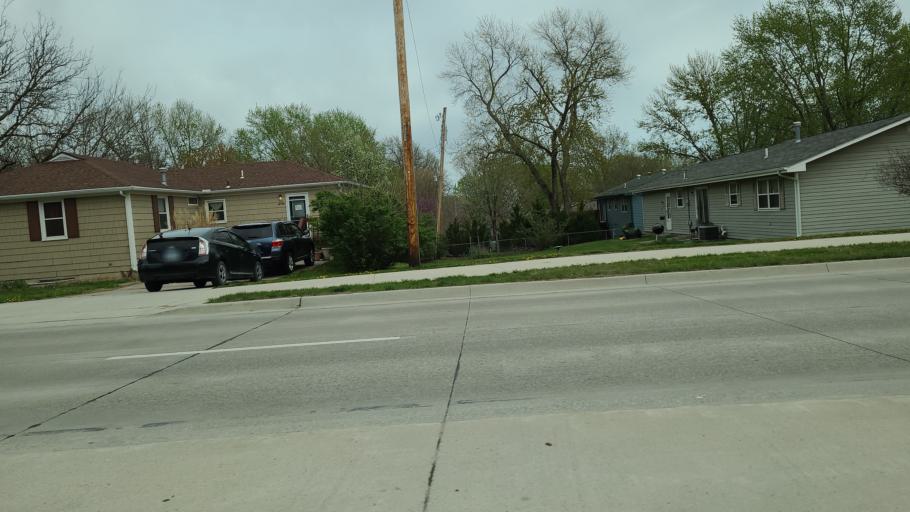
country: US
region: Kansas
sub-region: Douglas County
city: Lawrence
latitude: 38.9683
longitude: -95.2813
